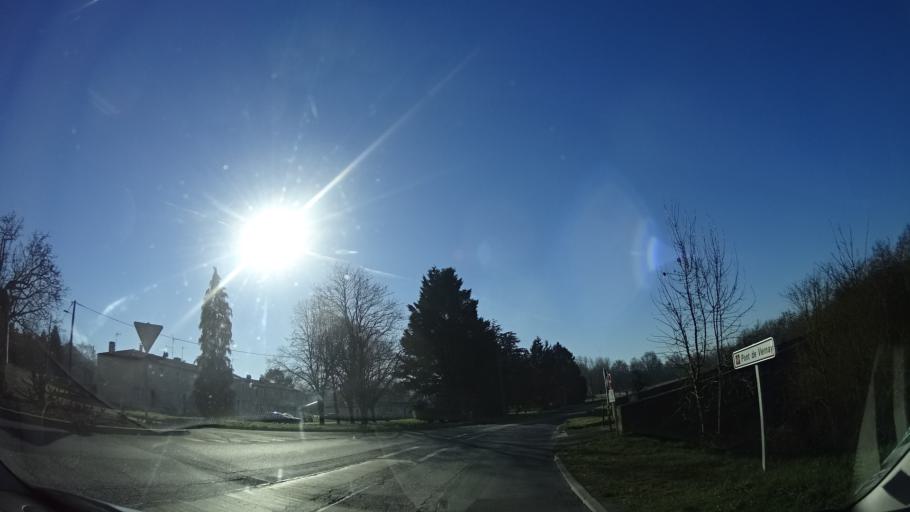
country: FR
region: Poitou-Charentes
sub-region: Departement des Deux-Sevres
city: Airvault
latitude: 46.8196
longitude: -0.1450
